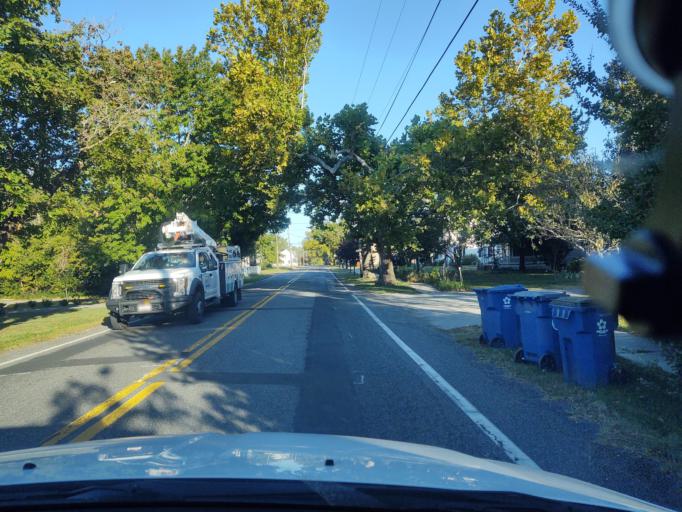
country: US
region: Maryland
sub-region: Queen Anne's County
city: Kingstown
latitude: 39.2393
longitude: -75.9204
